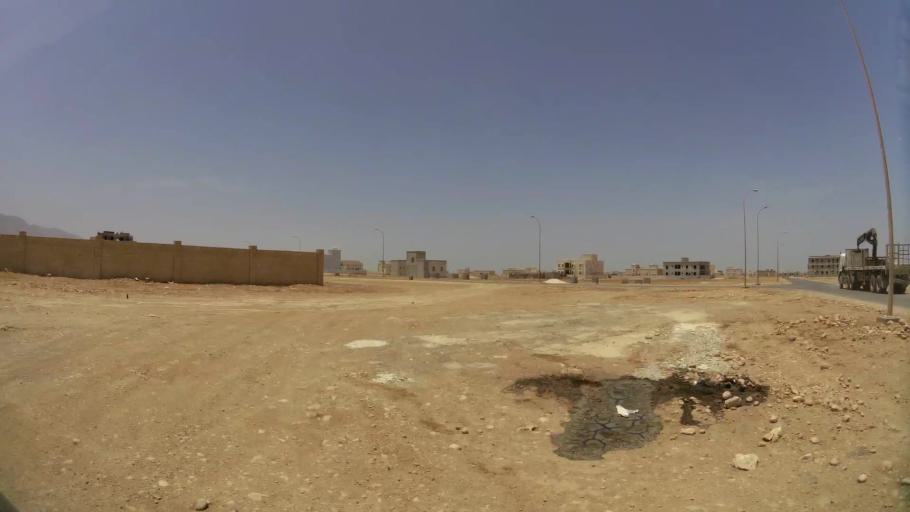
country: OM
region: Zufar
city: Salalah
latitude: 17.0955
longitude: 54.2107
